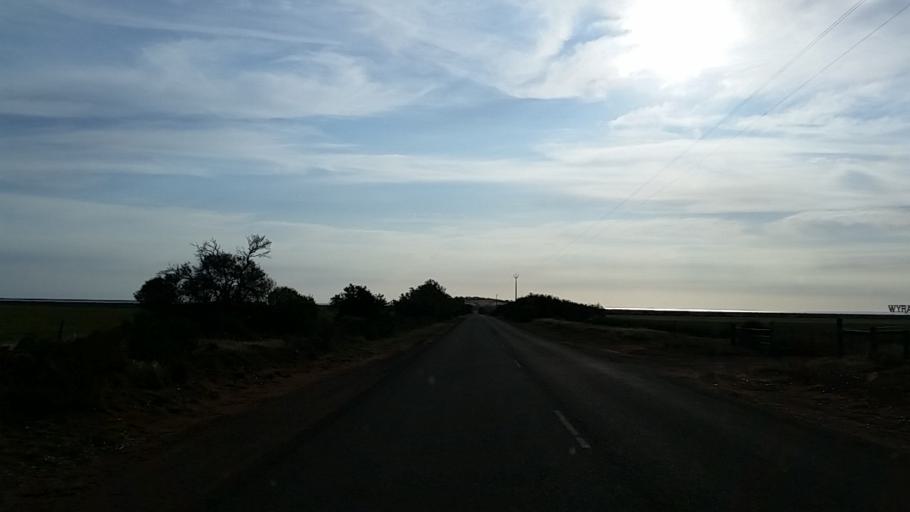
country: AU
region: South Australia
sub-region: Port Pirie City and Dists
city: Port Pirie
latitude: -33.1039
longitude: 138.0652
